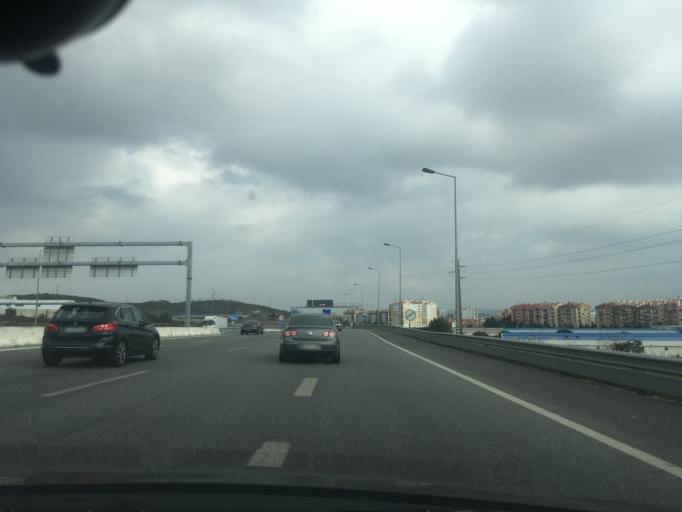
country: PT
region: Lisbon
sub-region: Sintra
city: Sintra
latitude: 38.7851
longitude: -9.3606
